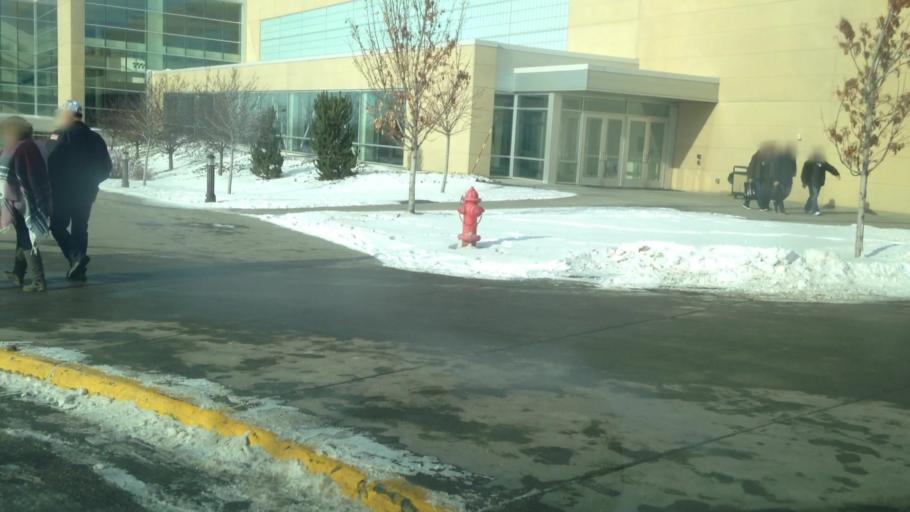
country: US
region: Idaho
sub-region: Madison County
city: Rexburg
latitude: 43.8178
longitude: -111.7838
